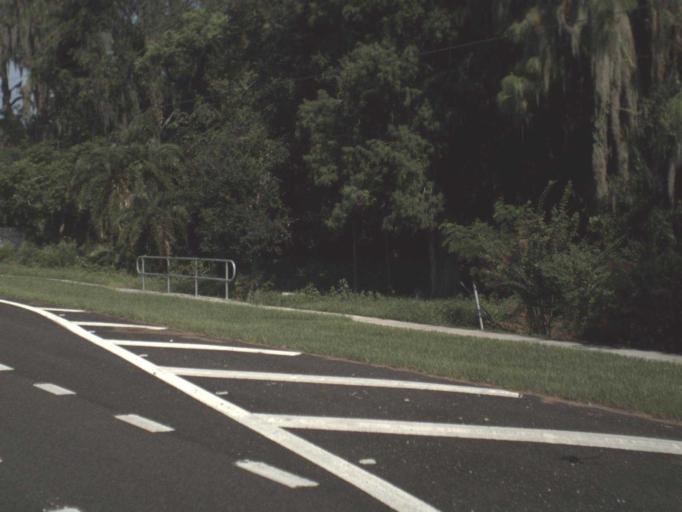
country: US
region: Florida
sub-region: Hillsborough County
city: Valrico
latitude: 27.9377
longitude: -82.1646
